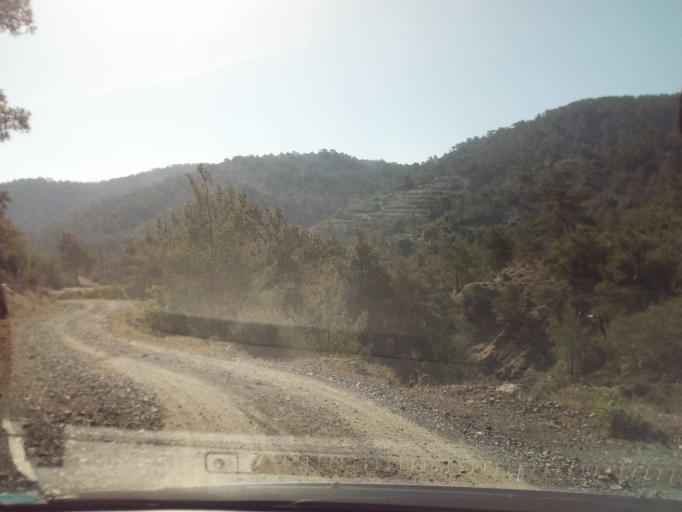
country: CY
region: Limassol
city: Pelendri
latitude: 34.8295
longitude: 33.0518
